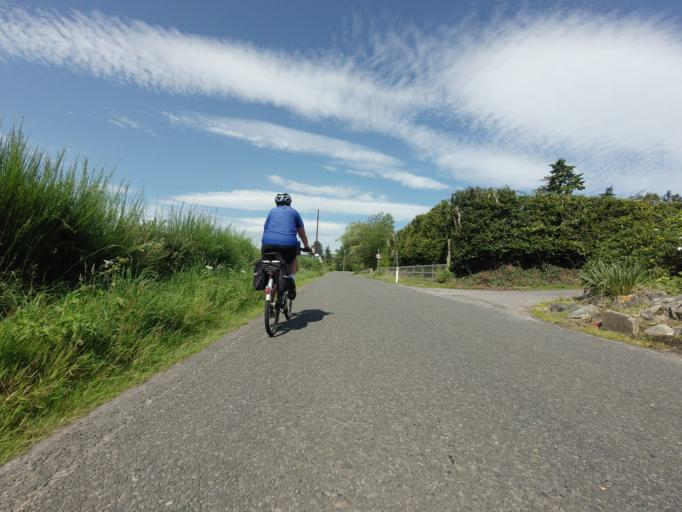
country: GB
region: Scotland
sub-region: Highland
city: Conon Bridge
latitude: 57.5398
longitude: -4.3303
